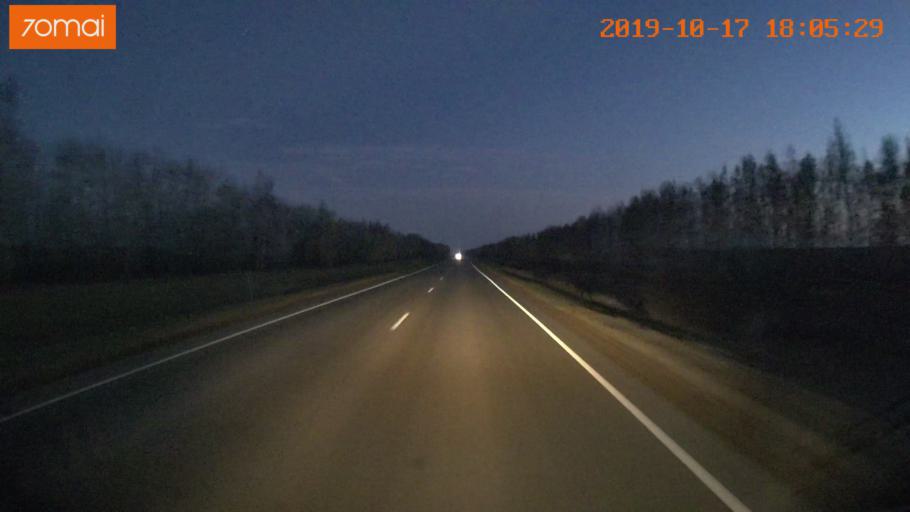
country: RU
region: Tula
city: Kurkino
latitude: 53.4658
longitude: 38.6446
